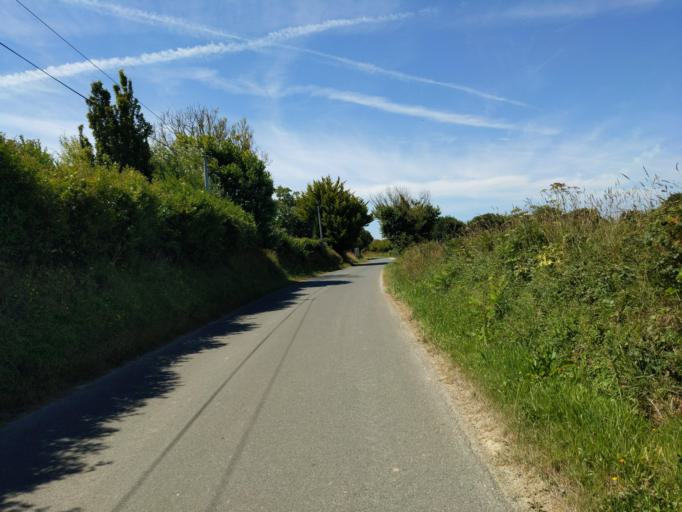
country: FR
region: Brittany
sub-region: Departement des Cotes-d'Armor
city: Pleumeur-Gautier
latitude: 48.8282
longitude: -3.1763
